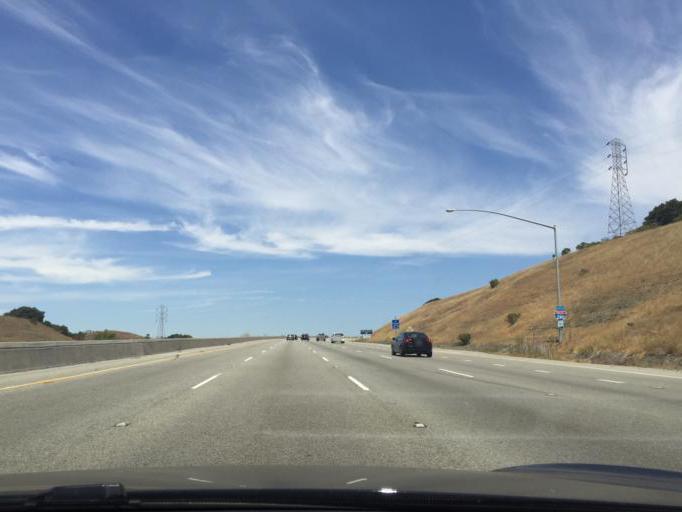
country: US
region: California
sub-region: San Mateo County
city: Emerald Lake Hills
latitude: 37.4724
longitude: -122.2958
